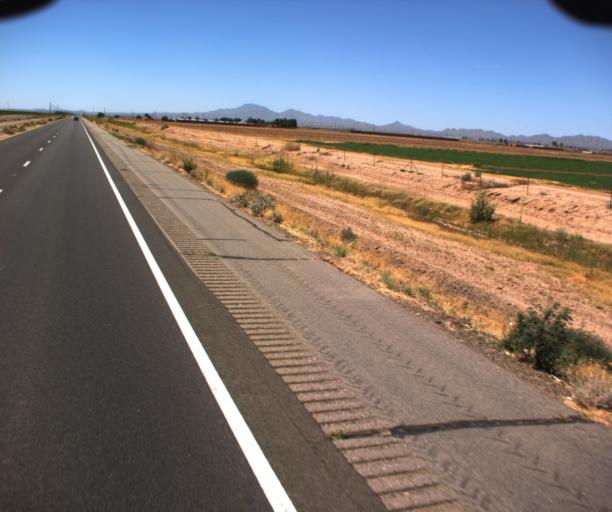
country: US
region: Arizona
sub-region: Pinal County
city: Maricopa
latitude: 32.9952
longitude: -112.0481
